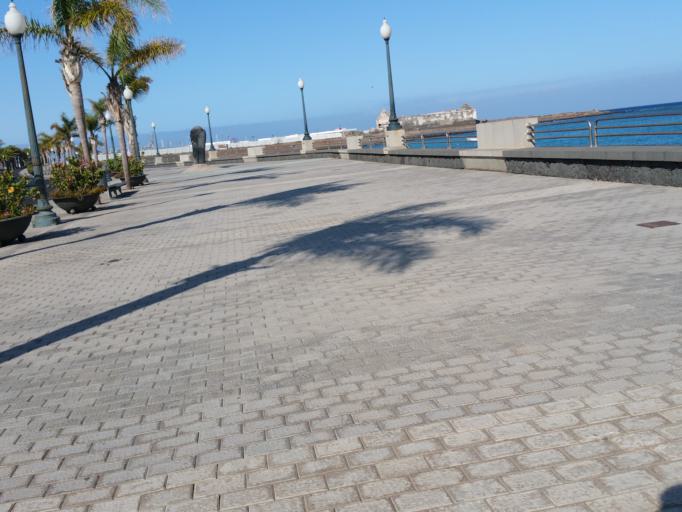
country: ES
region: Canary Islands
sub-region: Provincia de Las Palmas
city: Arrecife
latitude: 28.9588
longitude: -13.5472
